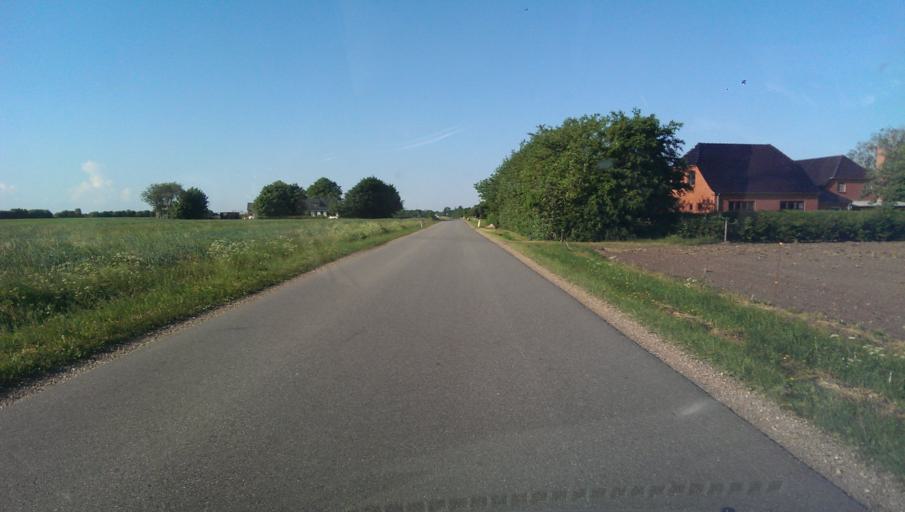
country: DK
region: South Denmark
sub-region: Esbjerg Kommune
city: Bramming
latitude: 55.5358
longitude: 8.6947
